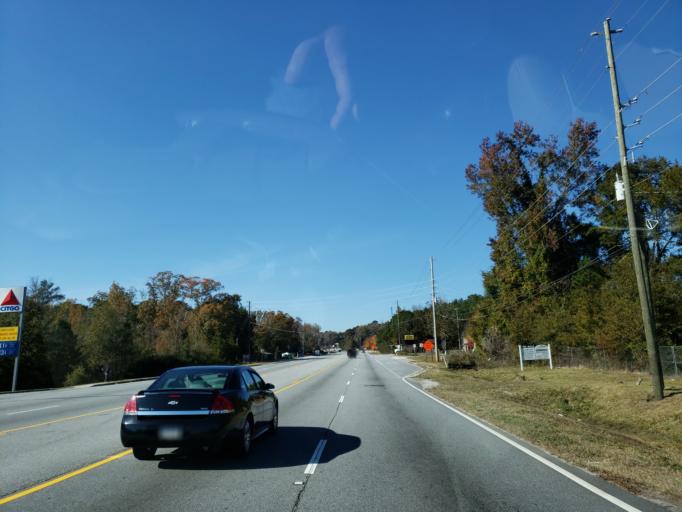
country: US
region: Georgia
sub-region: Cobb County
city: Mableton
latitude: 33.7838
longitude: -84.5408
